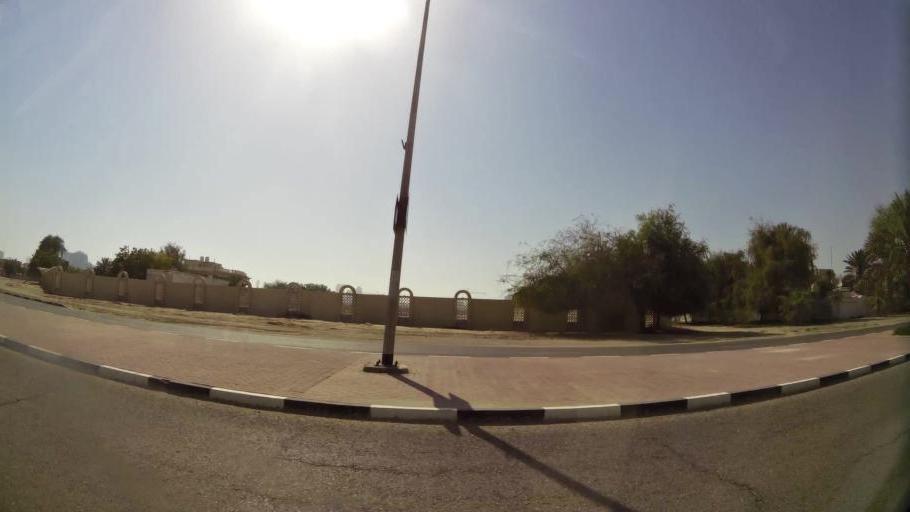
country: AE
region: Ajman
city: Ajman
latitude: 25.4096
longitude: 55.4661
